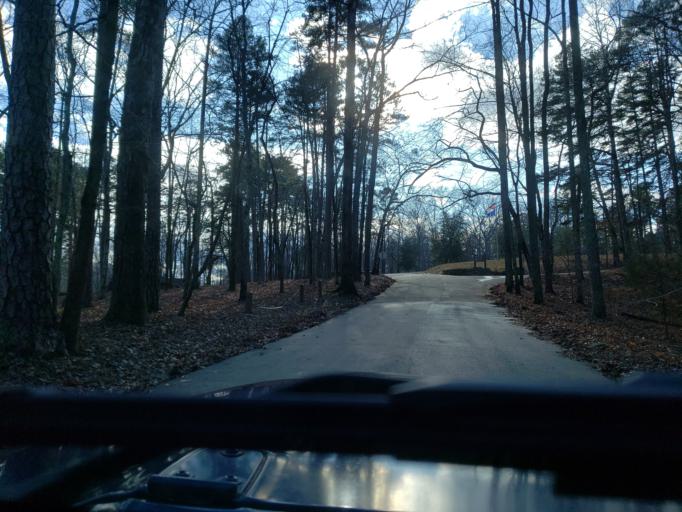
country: US
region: North Carolina
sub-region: Cleveland County
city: Kings Mountain
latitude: 35.1500
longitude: -81.3448
